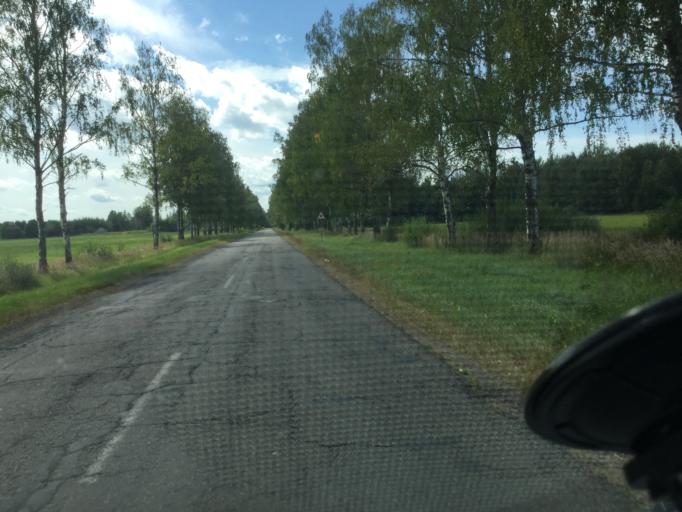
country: BY
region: Vitebsk
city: Chashniki
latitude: 55.3066
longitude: 29.4004
